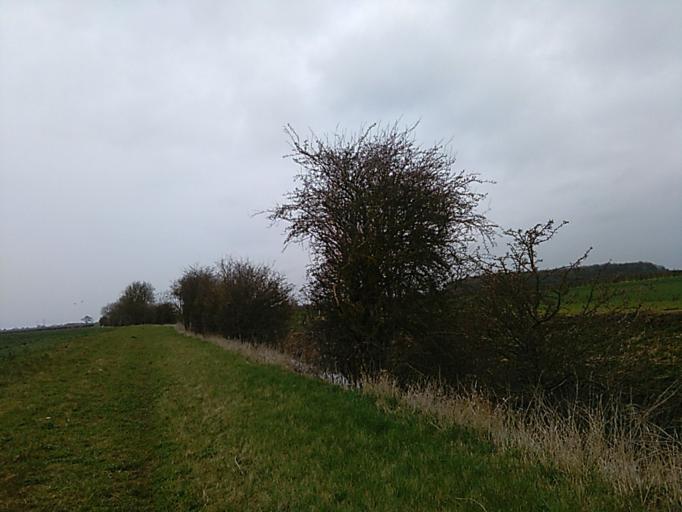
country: GB
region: England
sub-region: Nottinghamshire
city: Bingham
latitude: 52.9200
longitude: -0.9341
